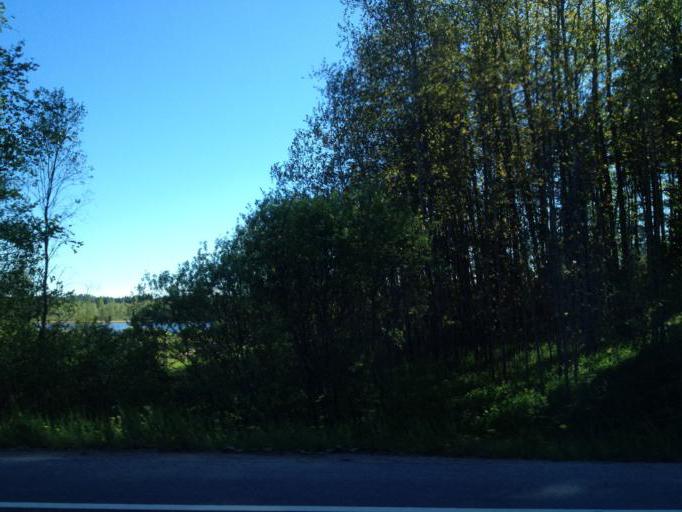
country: FI
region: Uusimaa
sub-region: Helsinki
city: Espoo
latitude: 60.2407
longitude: 24.5907
